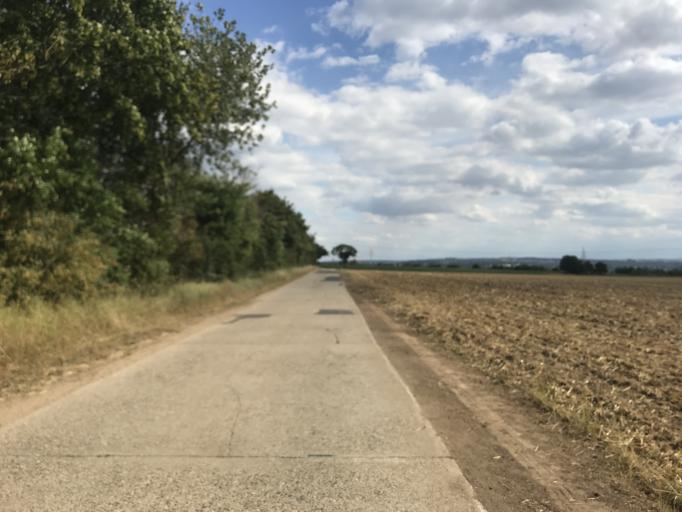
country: DE
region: Hesse
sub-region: Regierungsbezirk Darmstadt
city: Hochheim am Main
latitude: 50.0362
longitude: 8.3036
